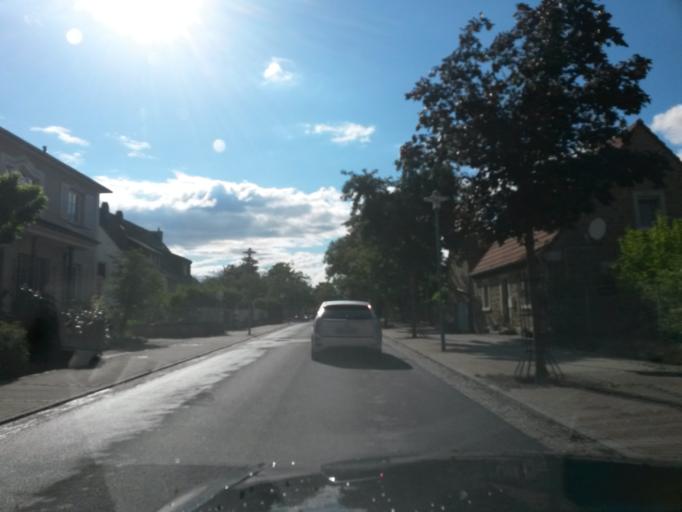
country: DE
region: Bavaria
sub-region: Regierungsbezirk Unterfranken
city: Rottendorf
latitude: 49.7907
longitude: 10.0215
